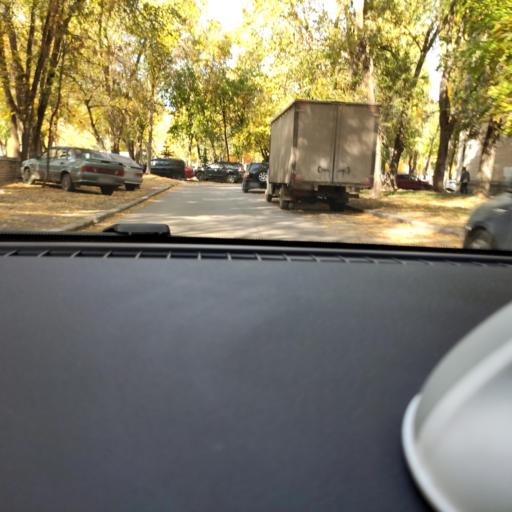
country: RU
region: Samara
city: Samara
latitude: 53.2232
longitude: 50.2440
